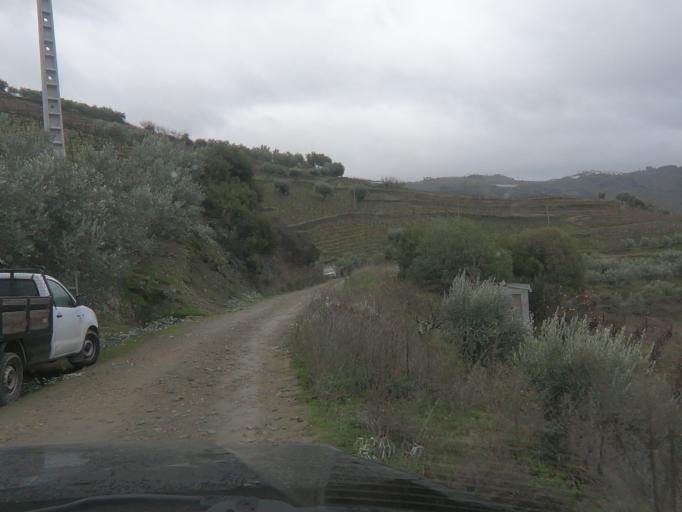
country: PT
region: Vila Real
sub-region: Santa Marta de Penaguiao
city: Santa Marta de Penaguiao
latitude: 41.2399
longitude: -7.7475
